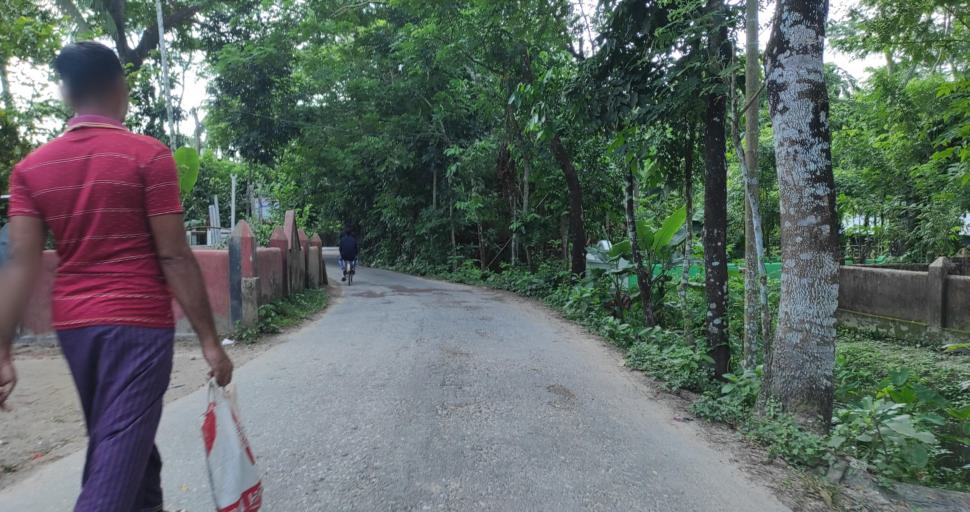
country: BD
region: Barisal
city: Gaurnadi
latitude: 22.8954
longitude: 90.1854
